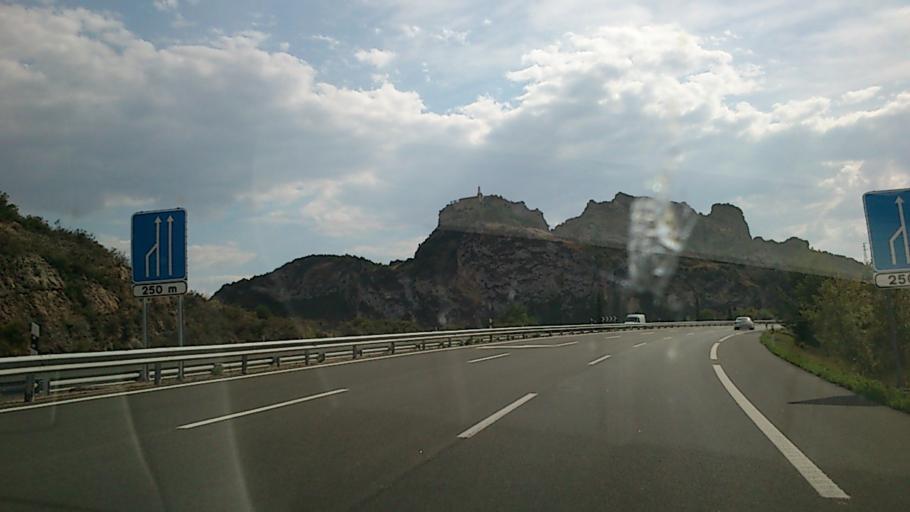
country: ES
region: La Rioja
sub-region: Provincia de La Rioja
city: Brinas
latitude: 42.6201
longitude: -2.8539
